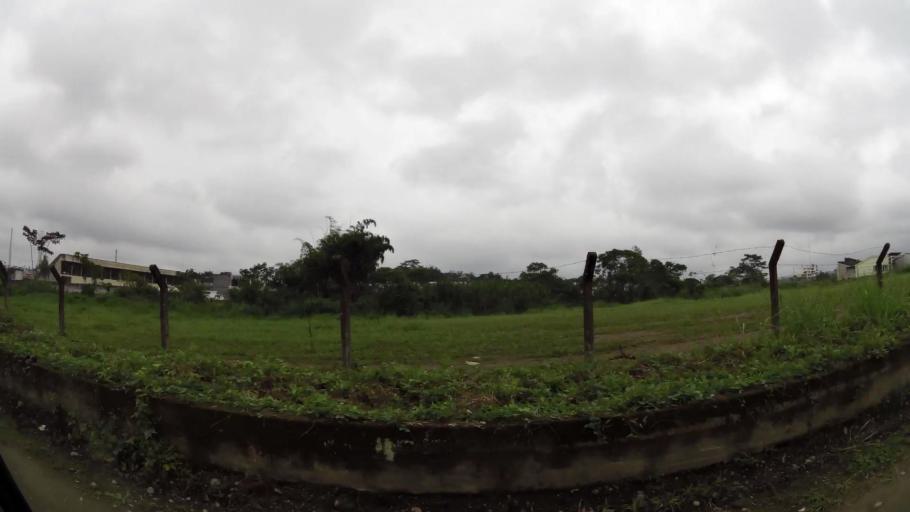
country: EC
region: Santo Domingo de los Tsachilas
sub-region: Canton Santo Domingo de los Colorados
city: Santo Domingo de los Colorados
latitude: -0.2512
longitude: -79.1468
